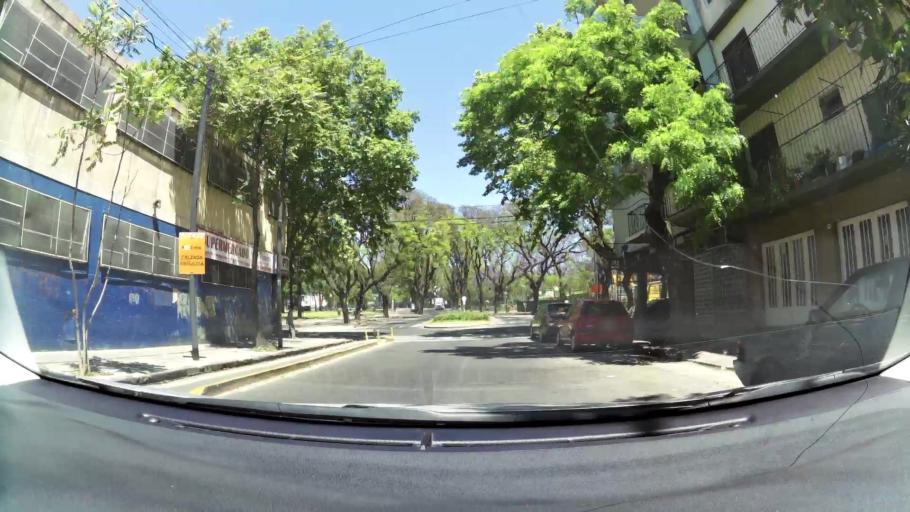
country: AR
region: Buenos Aires F.D.
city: Buenos Aires
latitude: -34.6396
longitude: -58.4049
